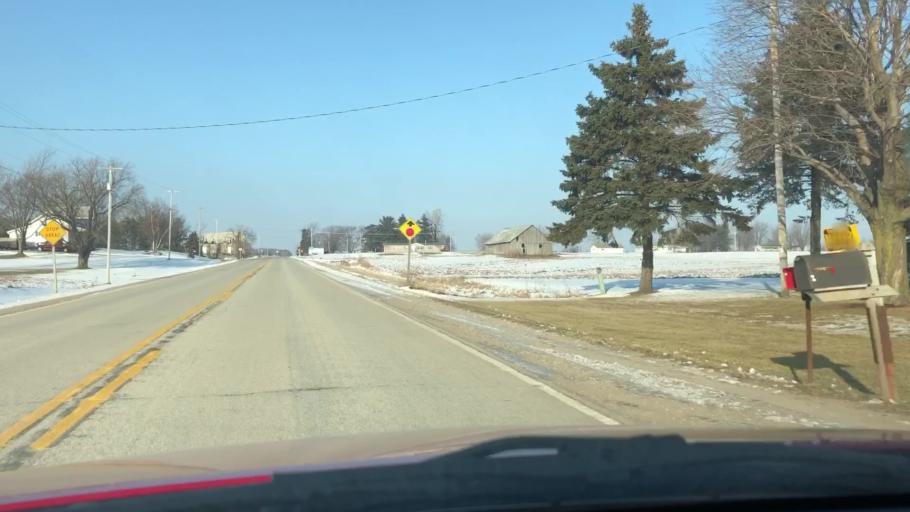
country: US
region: Wisconsin
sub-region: Outagamie County
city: Black Creek
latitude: 44.4115
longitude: -88.3745
